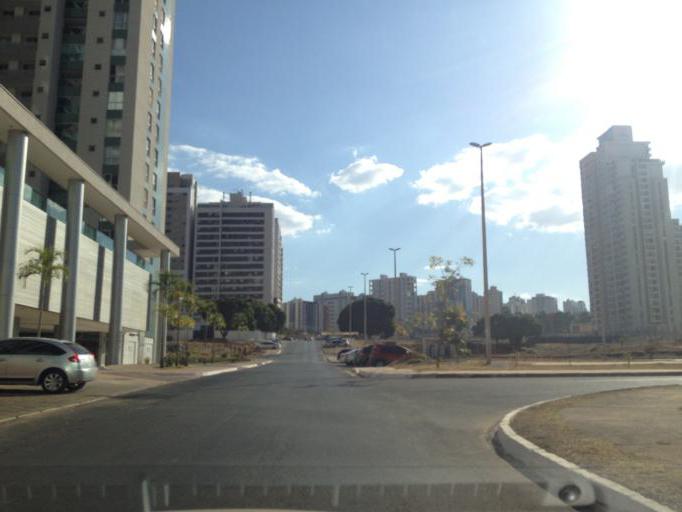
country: BR
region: Federal District
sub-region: Brasilia
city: Brasilia
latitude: -15.8408
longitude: -48.0279
